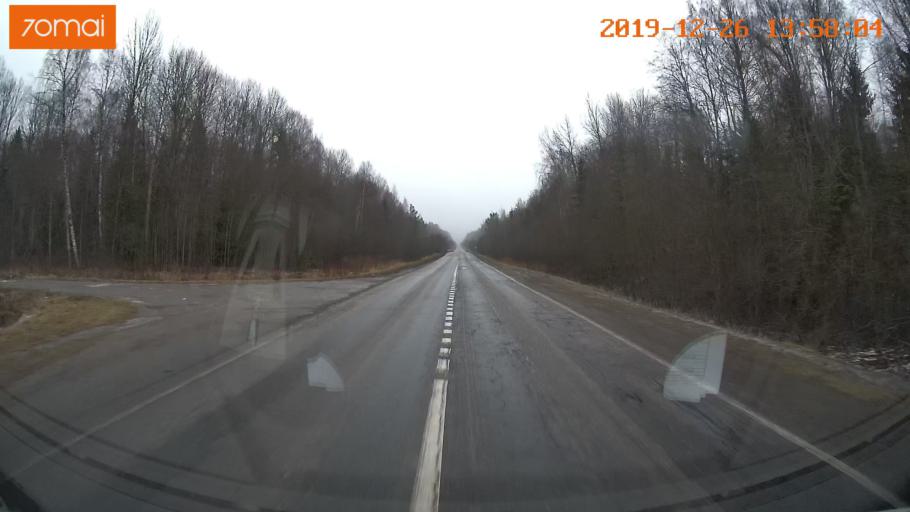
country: RU
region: Jaroslavl
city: Poshekhon'ye
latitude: 58.5772
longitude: 38.6927
